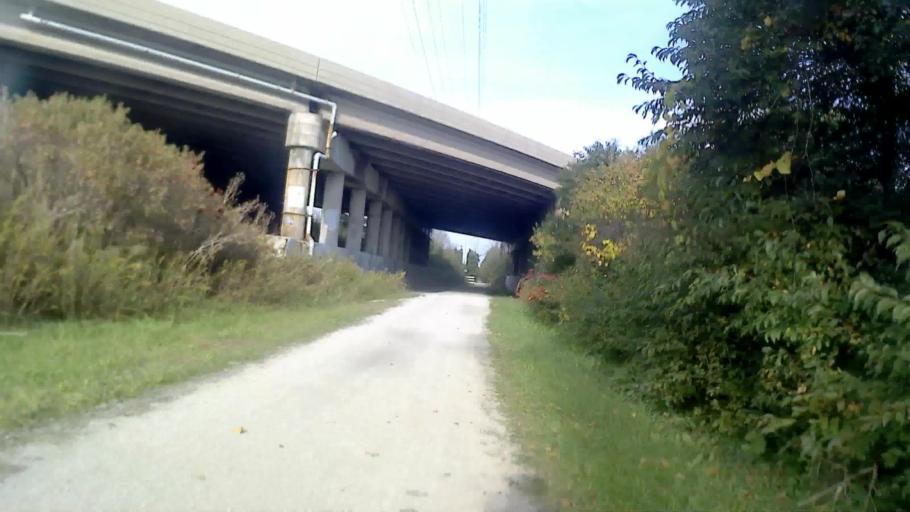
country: US
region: Illinois
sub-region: DuPage County
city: Warrenville
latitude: 41.8021
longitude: -88.2179
